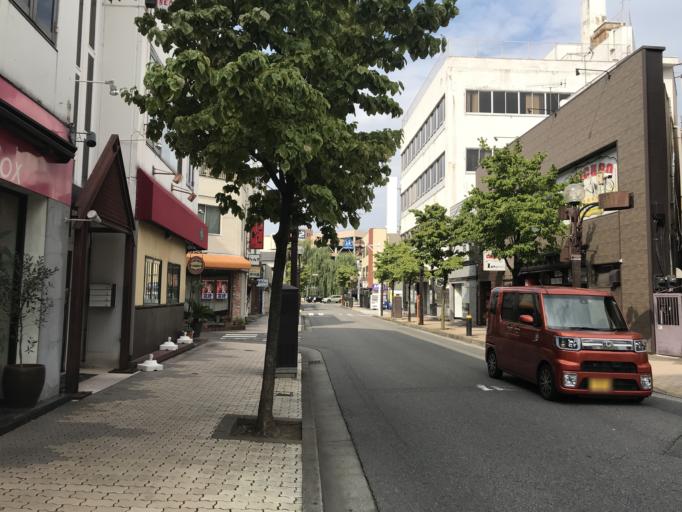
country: JP
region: Gunma
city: Maebashi-shi
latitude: 36.3922
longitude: 139.0721
